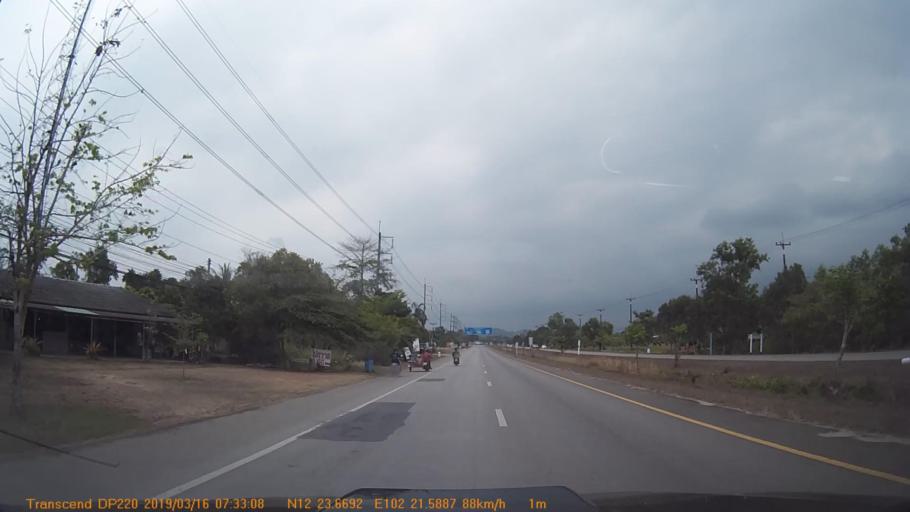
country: TH
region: Trat
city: Khao Saming
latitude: 12.3867
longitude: 102.3707
